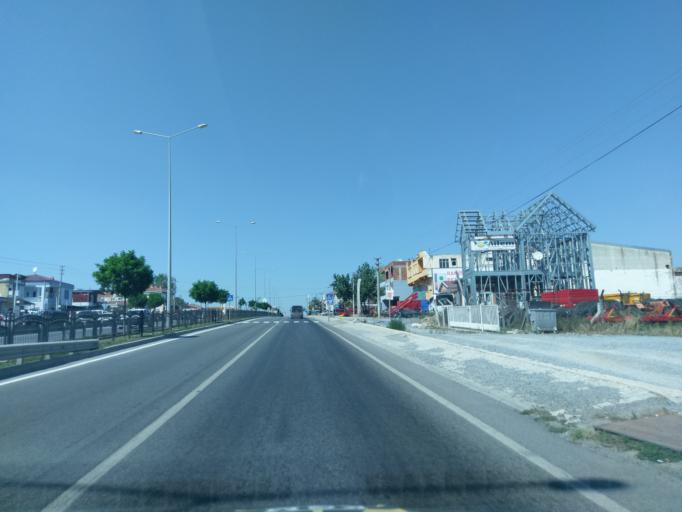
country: TR
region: Samsun
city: Bafra
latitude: 41.5466
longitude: 35.9285
